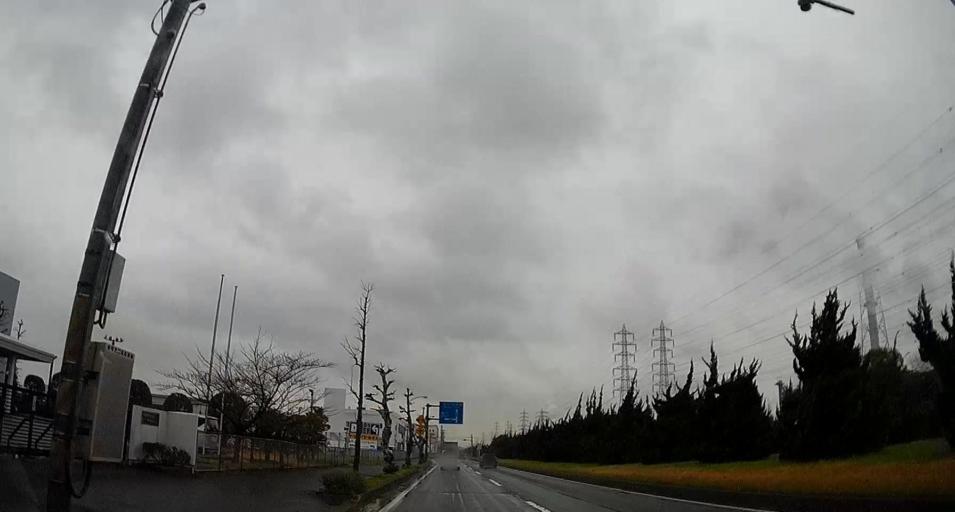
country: JP
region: Chiba
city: Ichihara
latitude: 35.4857
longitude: 140.0397
